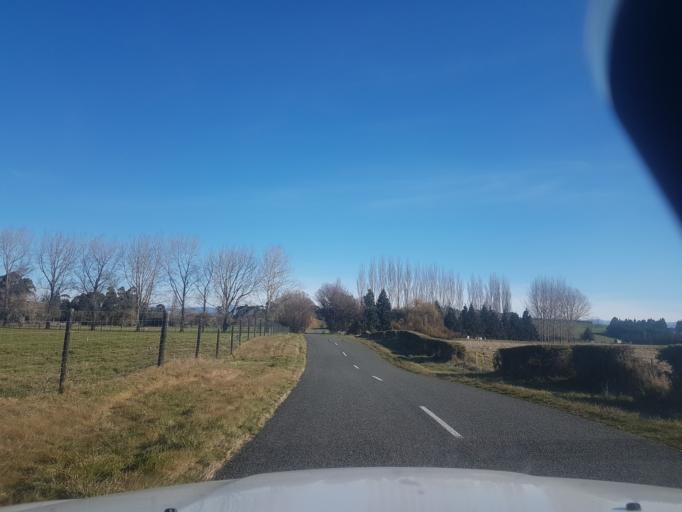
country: NZ
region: Canterbury
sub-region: Timaru District
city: Pleasant Point
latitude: -44.2450
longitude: 171.0905
